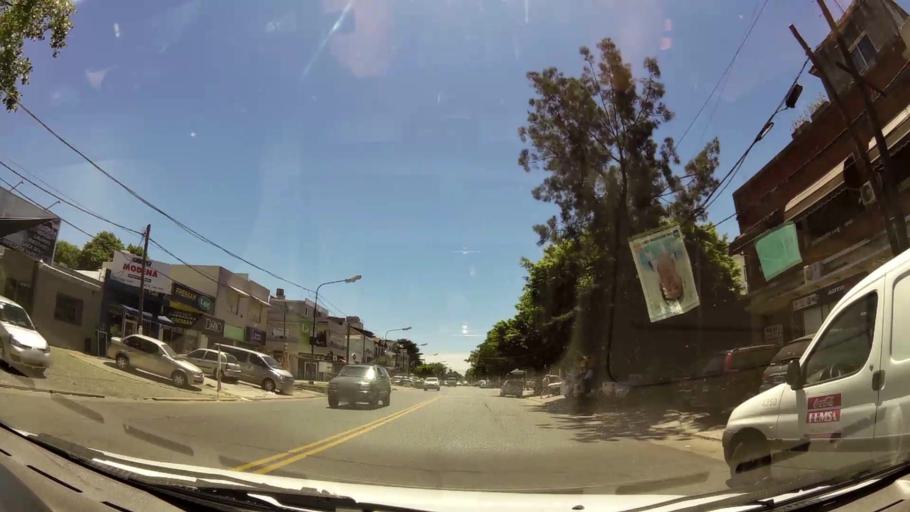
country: AR
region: Buenos Aires
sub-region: Partido de San Isidro
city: San Isidro
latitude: -34.4976
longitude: -58.5202
